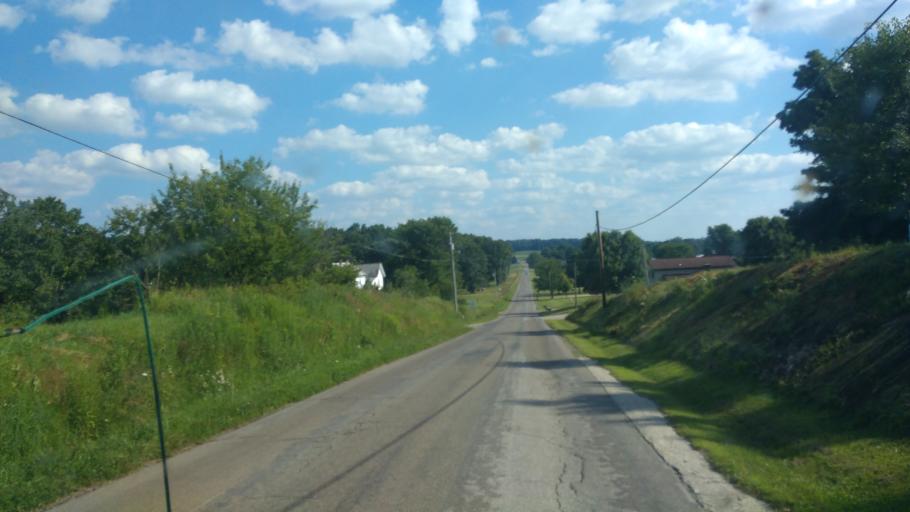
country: US
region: Ohio
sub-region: Wayne County
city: Apple Creek
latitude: 40.7386
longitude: -81.8438
